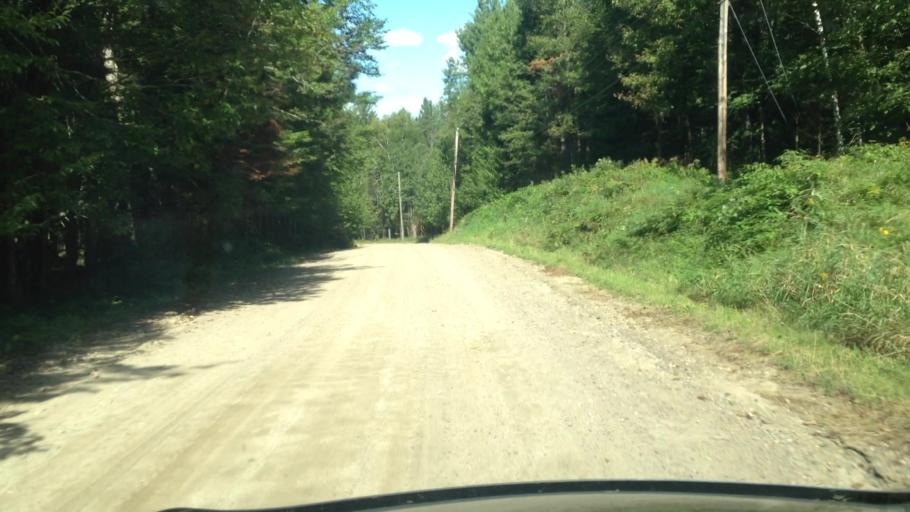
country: CA
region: Quebec
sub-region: Laurentides
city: Mont-Tremblant
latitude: 45.9441
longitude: -74.5892
